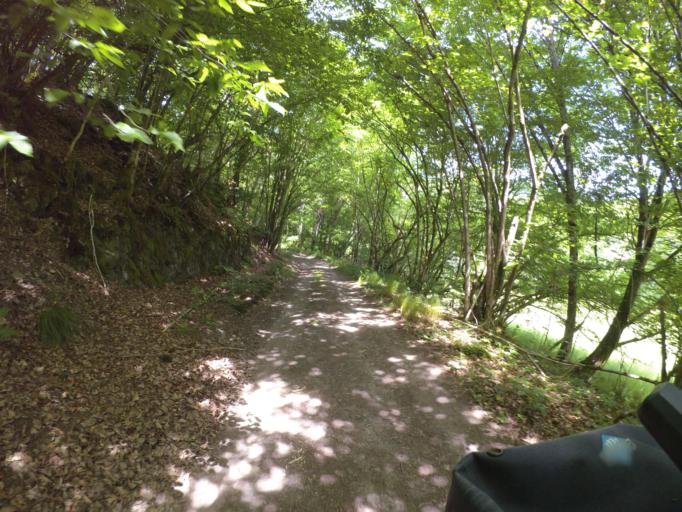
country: DE
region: Rheinland-Pfalz
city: Etgert
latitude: 49.7963
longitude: 7.0246
